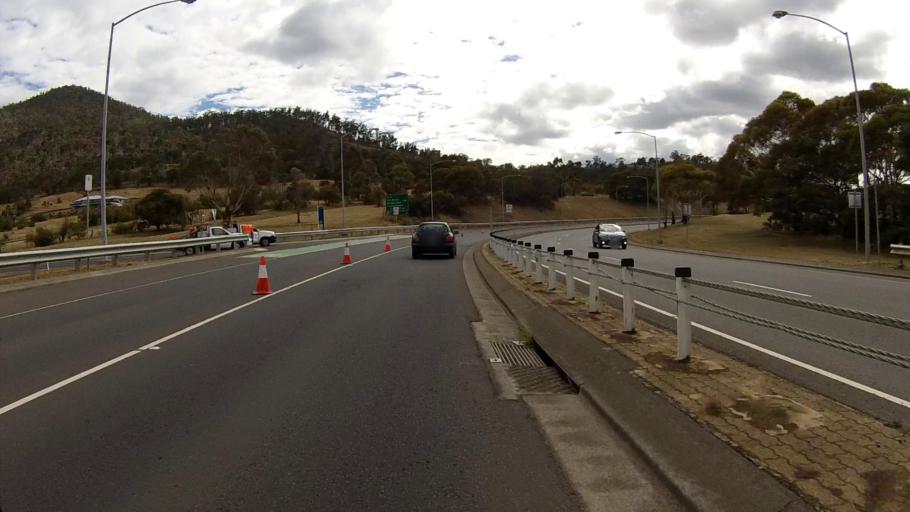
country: AU
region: Tasmania
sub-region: Glenorchy
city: Lutana
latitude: -42.8139
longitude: 147.3114
